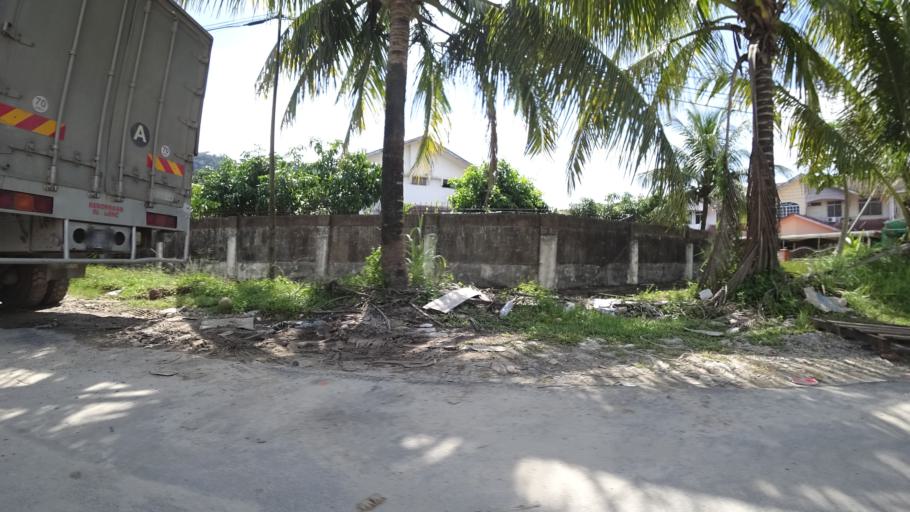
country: MY
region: Sarawak
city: Limbang
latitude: 4.7424
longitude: 115.0000
